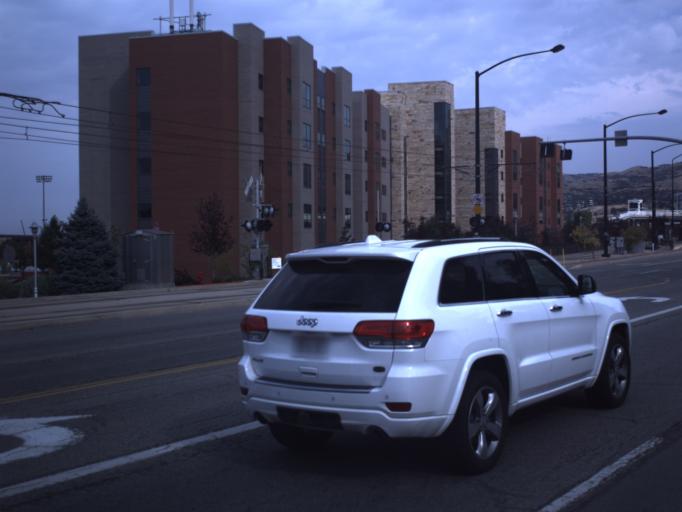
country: US
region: Utah
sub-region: Salt Lake County
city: Salt Lake City
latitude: 40.7630
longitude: -111.8357
